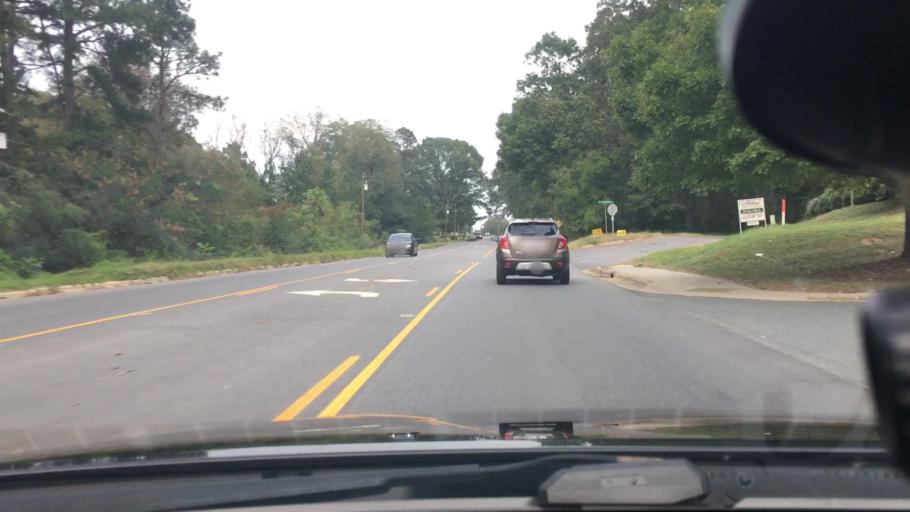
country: US
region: North Carolina
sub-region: Montgomery County
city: Troy
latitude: 35.3506
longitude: -79.9079
